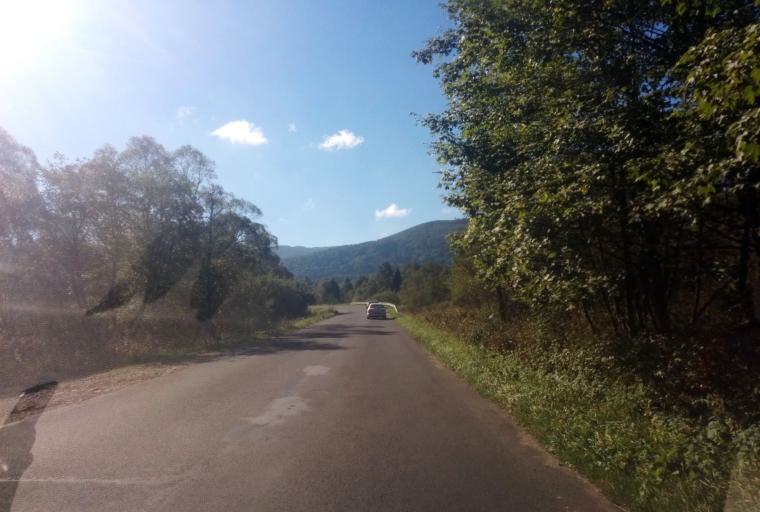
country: PL
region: Subcarpathian Voivodeship
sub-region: Powiat leski
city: Cisna
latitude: 49.2056
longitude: 22.3631
